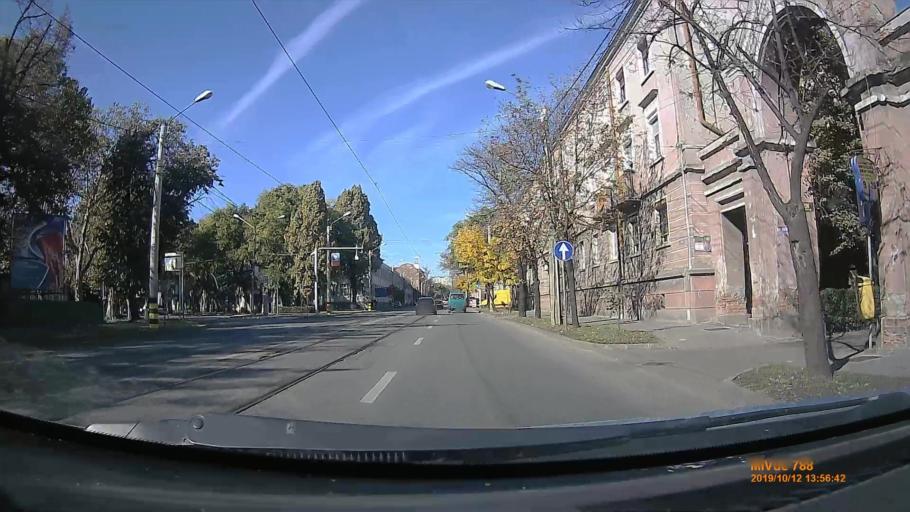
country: RO
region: Bihor
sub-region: Comuna Biharea
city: Oradea
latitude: 47.0637
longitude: 21.9379
